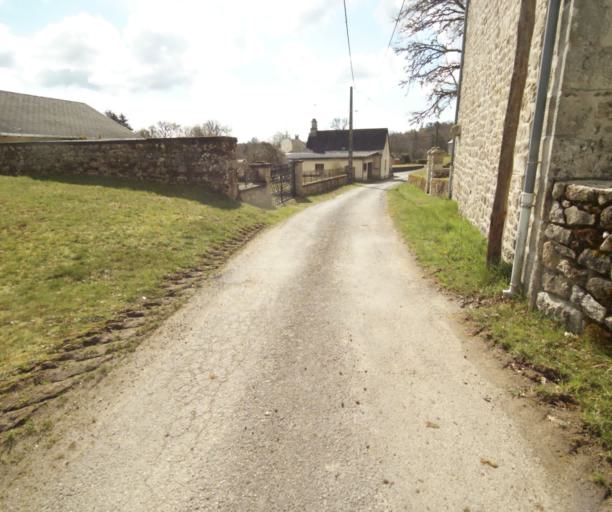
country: FR
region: Limousin
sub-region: Departement de la Correze
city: Argentat
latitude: 45.2384
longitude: 1.9544
